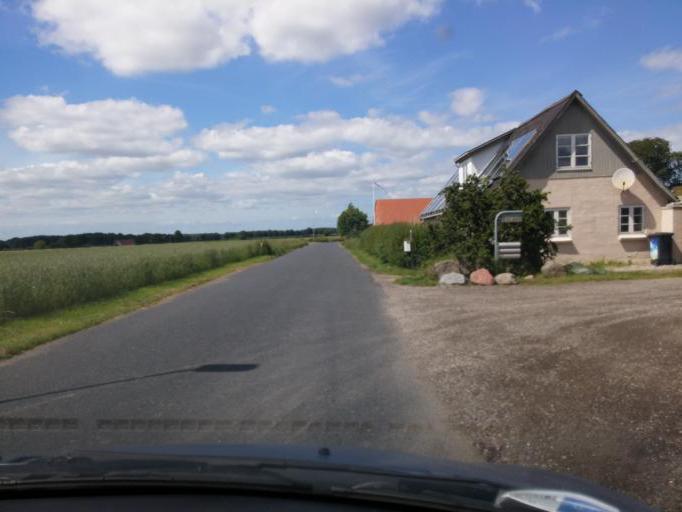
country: DK
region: South Denmark
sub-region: Kerteminde Kommune
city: Munkebo
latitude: 55.4122
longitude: 10.5779
